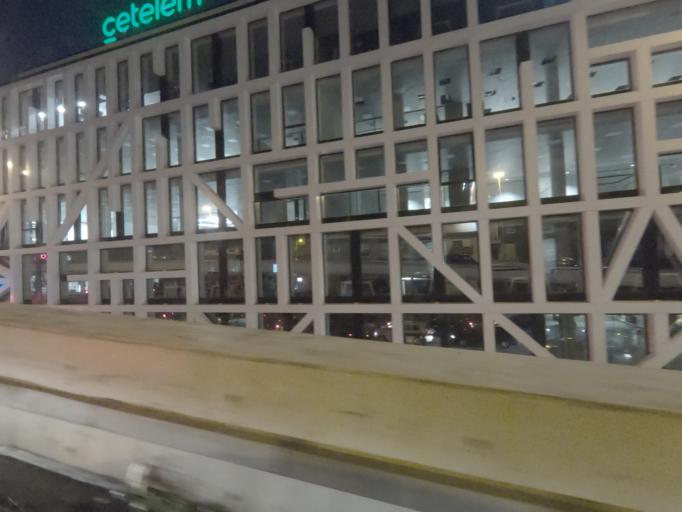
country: PT
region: Porto
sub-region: Matosinhos
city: Senhora da Hora
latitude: 41.1797
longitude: -8.6528
